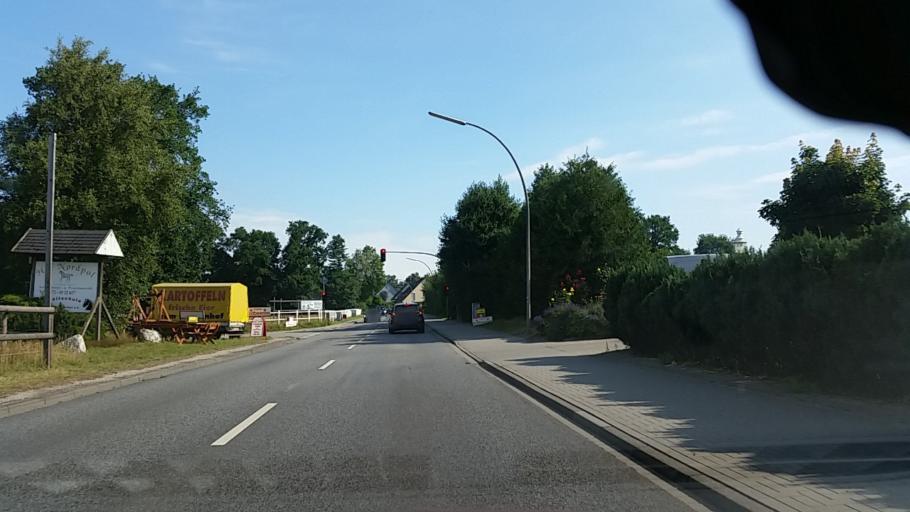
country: DE
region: Hamburg
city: Langenhorn
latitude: 53.7005
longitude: 10.0277
